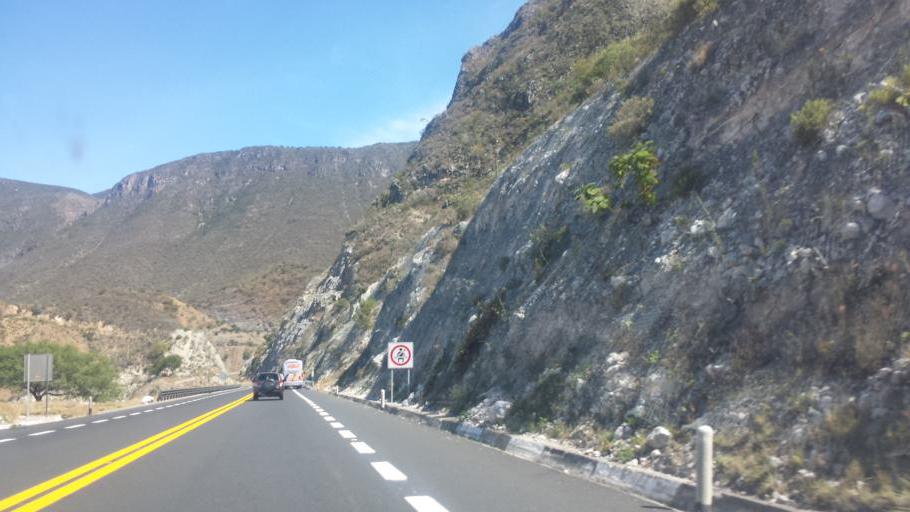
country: MX
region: Puebla
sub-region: San Jose Miahuatlan
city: San Pedro Tetitlan
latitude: 18.0883
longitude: -97.3485
